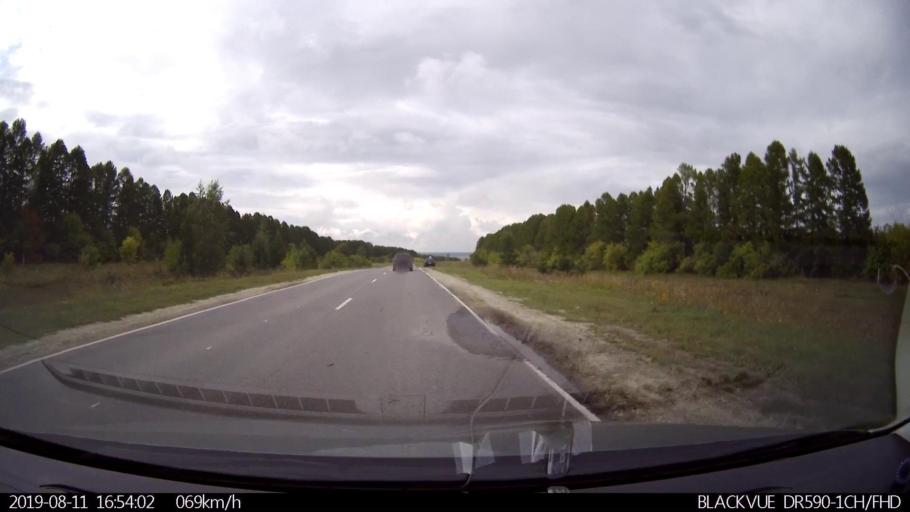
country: RU
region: Ulyanovsk
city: Mayna
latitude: 54.2685
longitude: 47.6677
